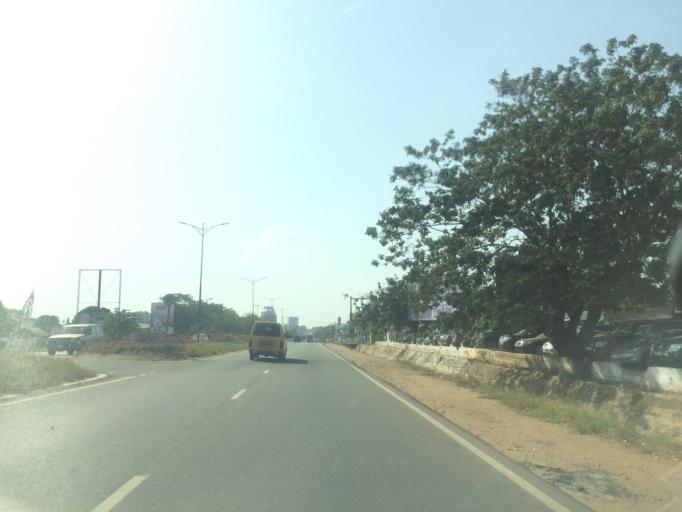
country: GH
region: Greater Accra
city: Accra
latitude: 5.5617
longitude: -0.1713
